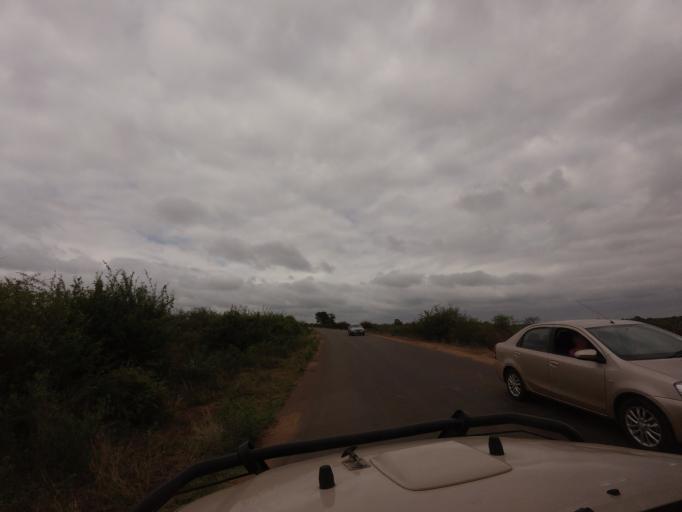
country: ZA
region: Mpumalanga
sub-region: Ehlanzeni District
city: Komatipoort
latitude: -25.1236
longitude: 31.9267
